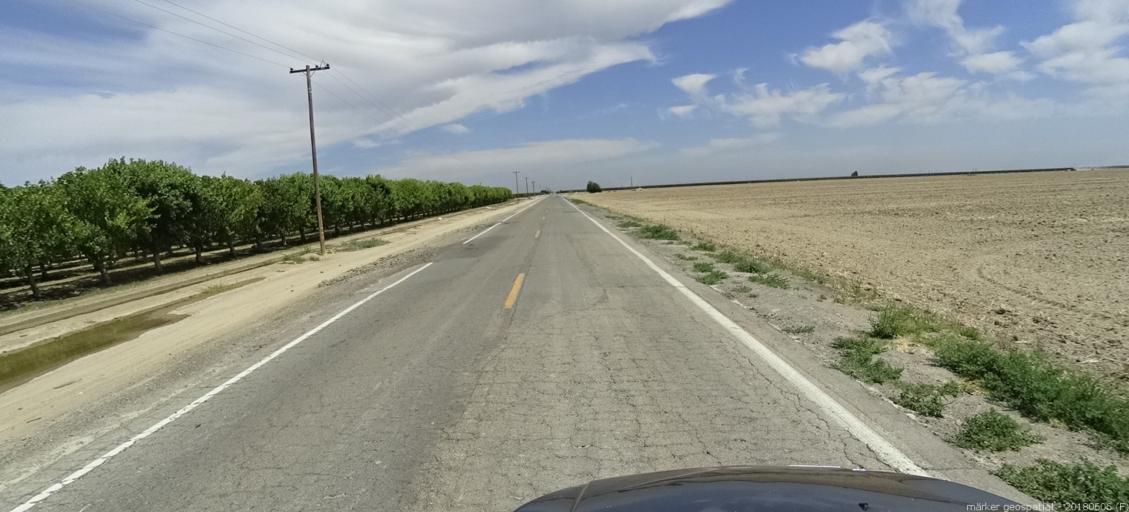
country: US
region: California
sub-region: Fresno County
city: Firebaugh
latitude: 36.9420
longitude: -120.3825
